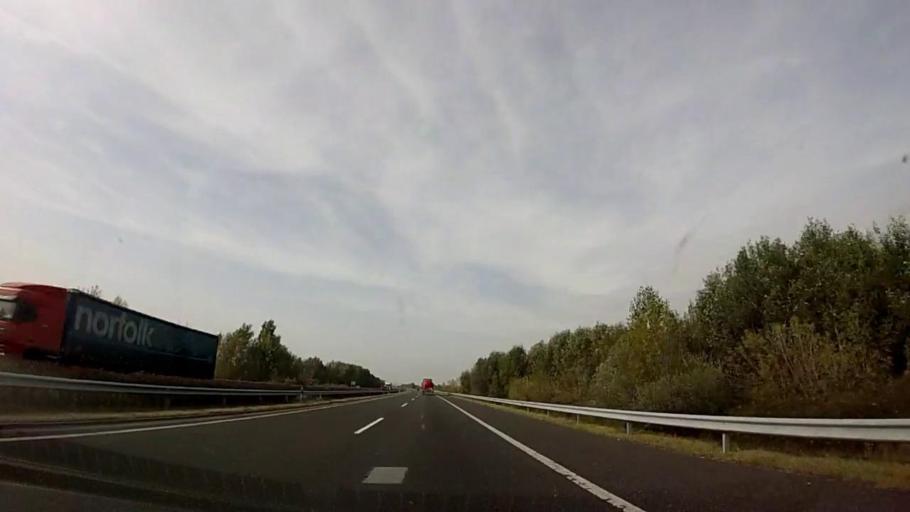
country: HU
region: Somogy
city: Balatonfenyves
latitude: 46.7013
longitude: 17.4719
